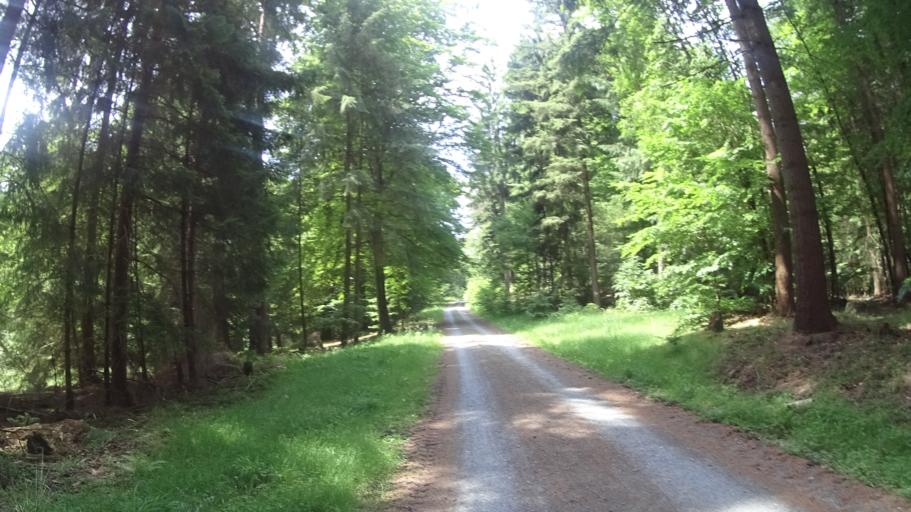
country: DE
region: Hesse
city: Rosenthal
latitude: 50.9508
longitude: 8.7948
